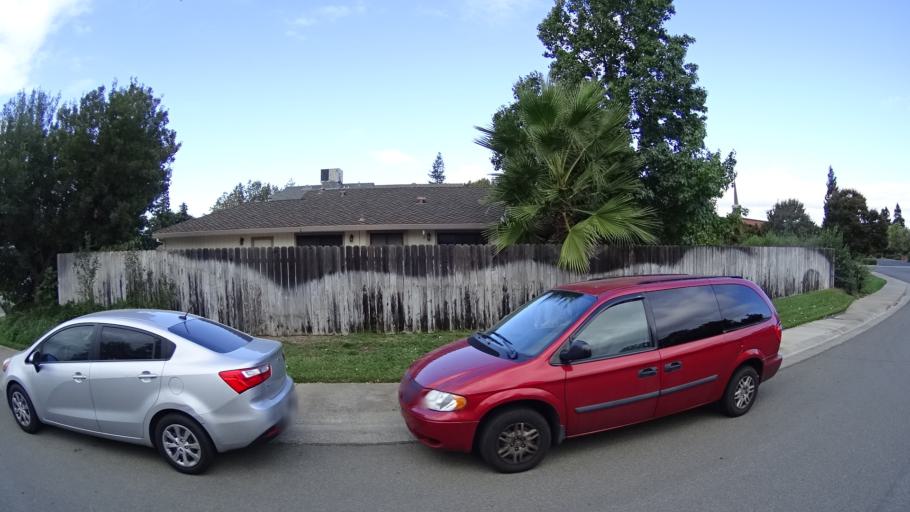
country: US
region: California
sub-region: Sacramento County
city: Laguna
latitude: 38.4182
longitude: -121.4244
